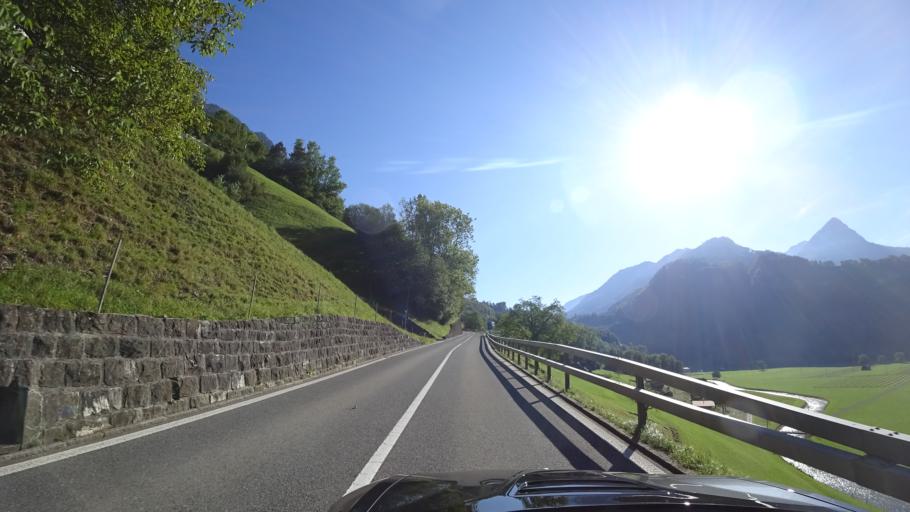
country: CH
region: Obwalden
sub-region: Obwalden
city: Giswil
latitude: 46.8280
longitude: 8.1851
